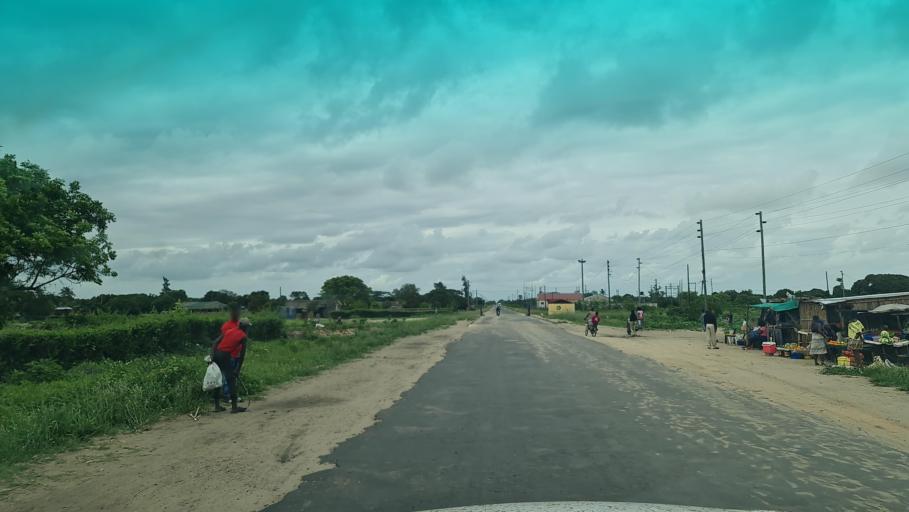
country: MZ
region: Maputo
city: Manhica
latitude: -25.4360
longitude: 32.7733
